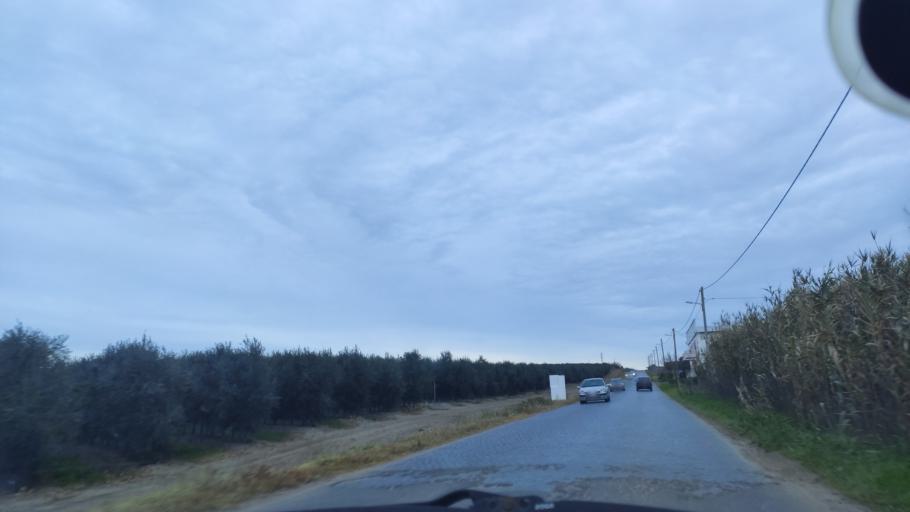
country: PT
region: Beja
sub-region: Beja
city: Ferreira do Alentejo
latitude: 38.0591
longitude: -8.1076
